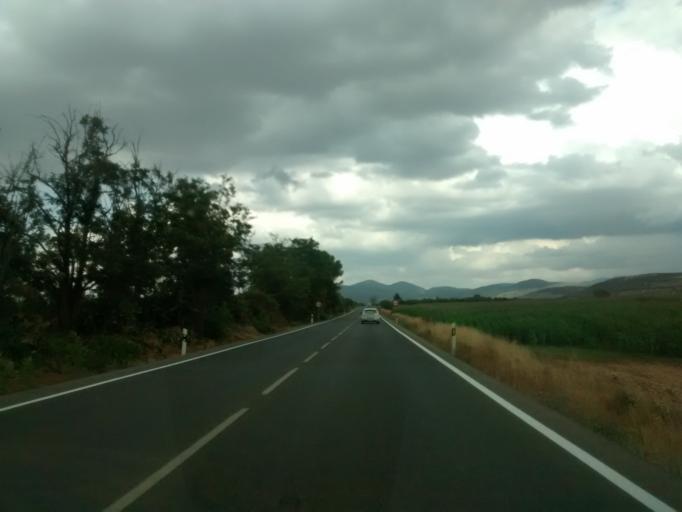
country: ES
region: Andalusia
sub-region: Provincia de Cadiz
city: Villamartin
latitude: 36.8736
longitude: -5.5899
